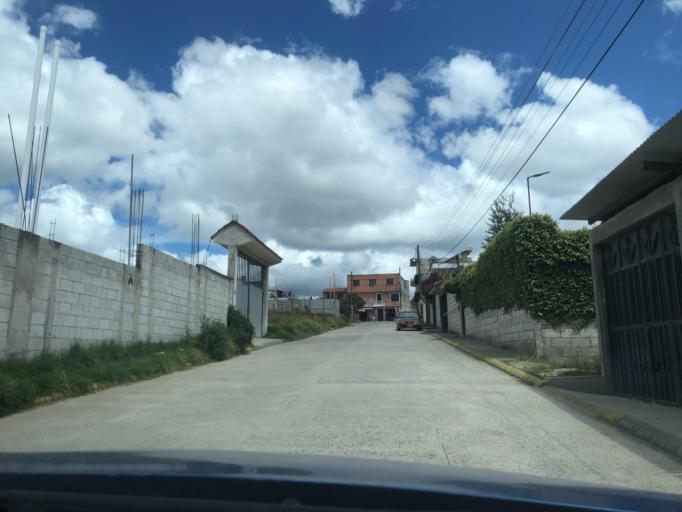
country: GT
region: Quetzaltenango
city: Quetzaltenango
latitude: 14.8406
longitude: -91.5444
